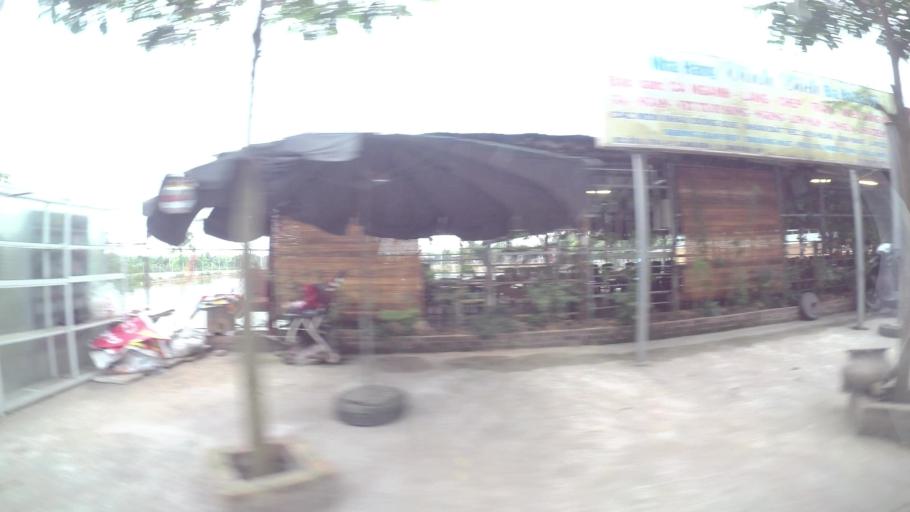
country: VN
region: Ha Noi
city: Trau Quy
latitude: 21.0682
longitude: 105.9185
